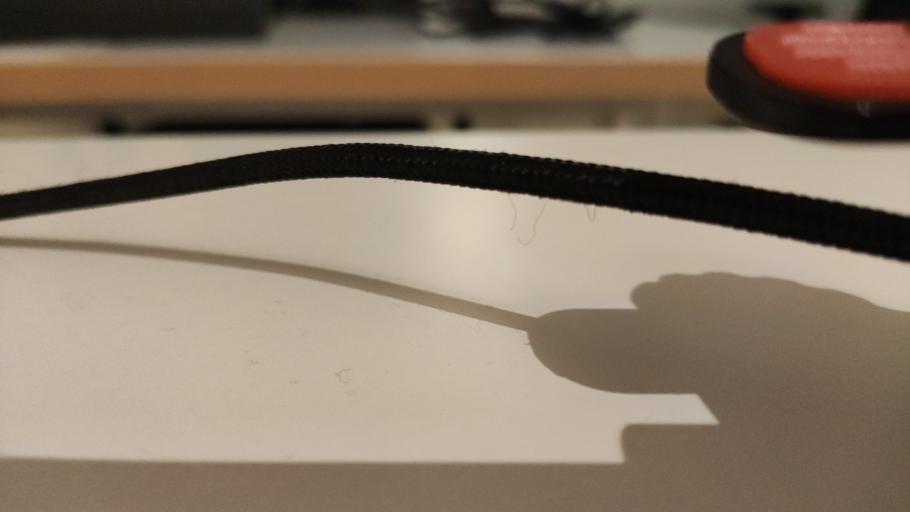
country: RU
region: Moskovskaya
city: Konstantinovo
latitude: 56.4186
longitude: 37.9855
